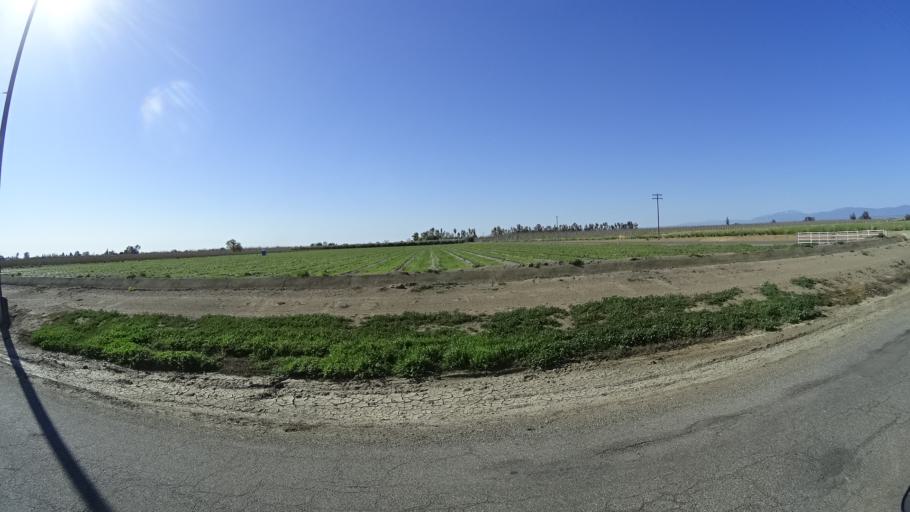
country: US
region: California
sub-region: Glenn County
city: Orland
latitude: 39.7441
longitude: -122.2381
